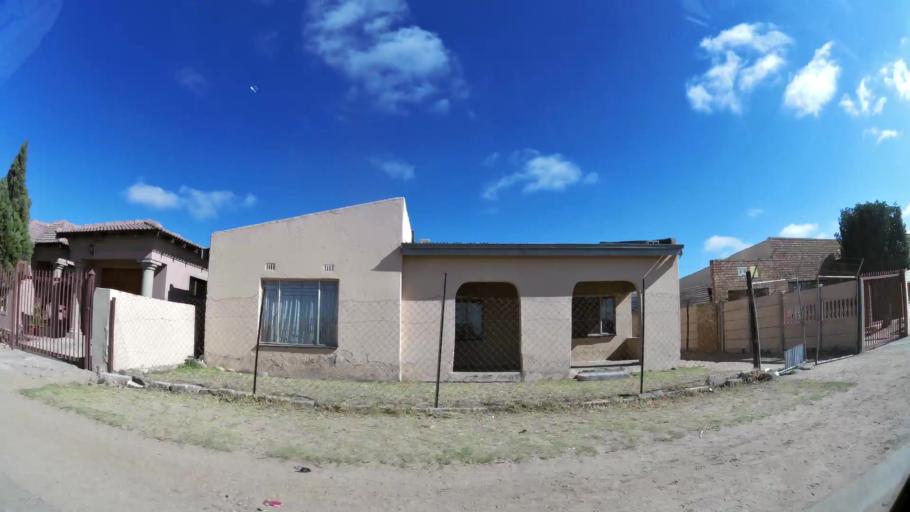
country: ZA
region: Limpopo
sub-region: Capricorn District Municipality
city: Polokwane
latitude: -23.8602
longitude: 29.3959
